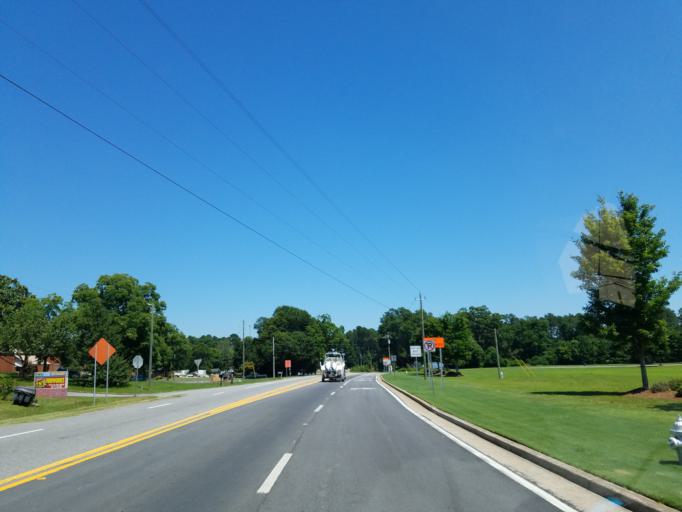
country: US
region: Georgia
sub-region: Forsyth County
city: Cumming
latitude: 34.2627
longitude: -84.0845
